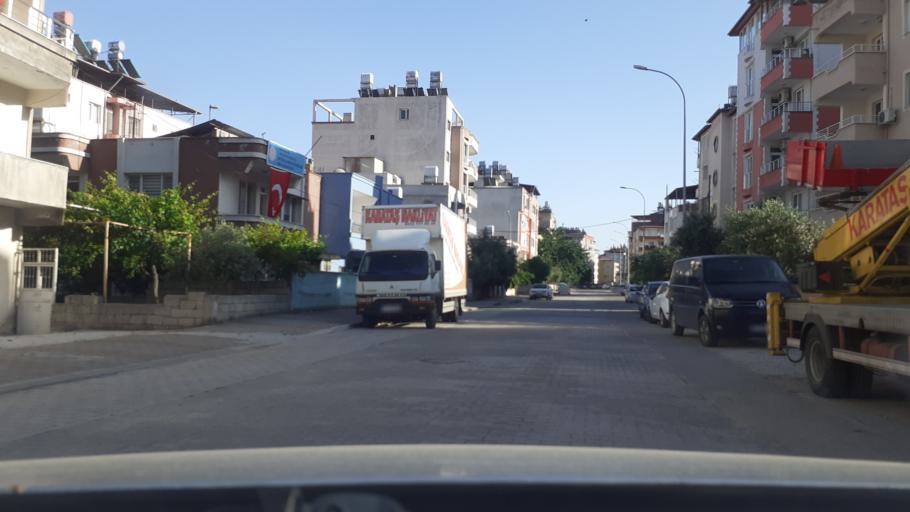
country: TR
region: Hatay
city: Kirikhan
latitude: 36.4972
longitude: 36.3654
